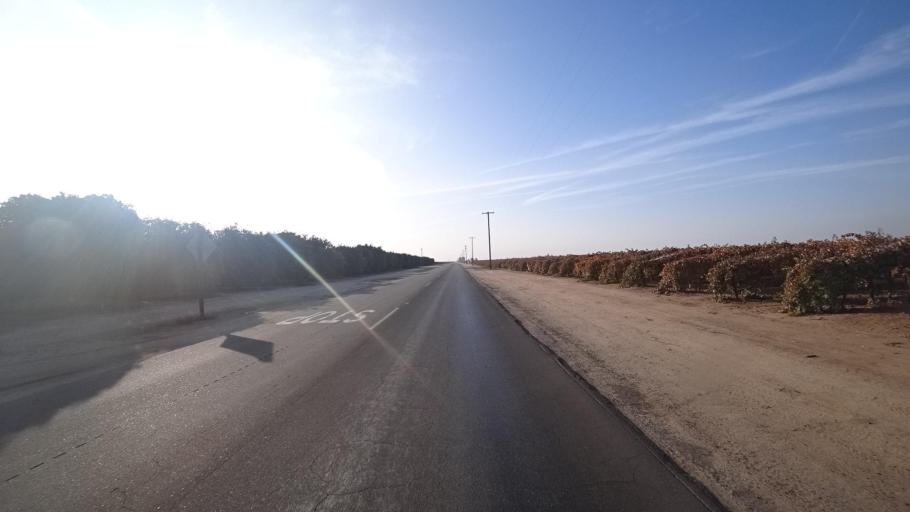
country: US
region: California
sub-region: Kern County
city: Delano
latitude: 35.7600
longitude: -119.1874
